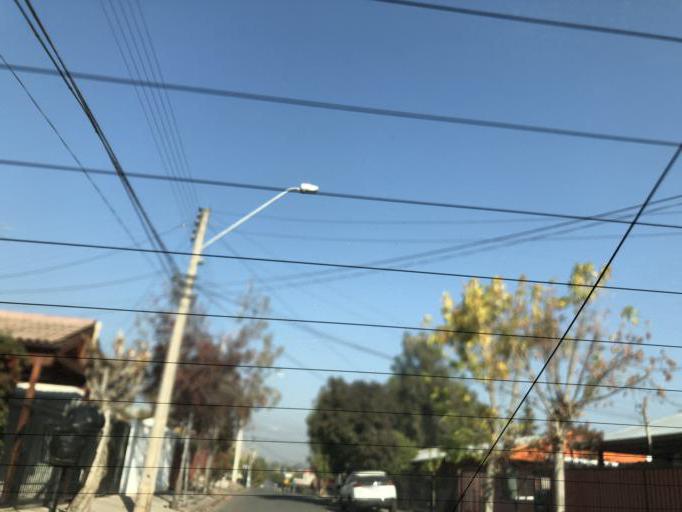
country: CL
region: Santiago Metropolitan
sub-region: Provincia de Cordillera
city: Puente Alto
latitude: -33.6123
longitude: -70.5590
